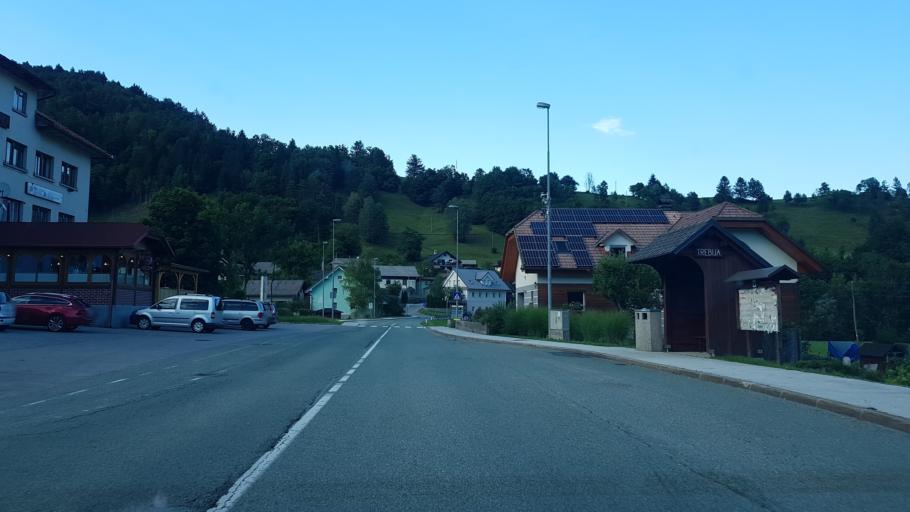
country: SI
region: Gorenja Vas-Poljane
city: Gorenja Vas
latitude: 46.0953
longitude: 14.1002
